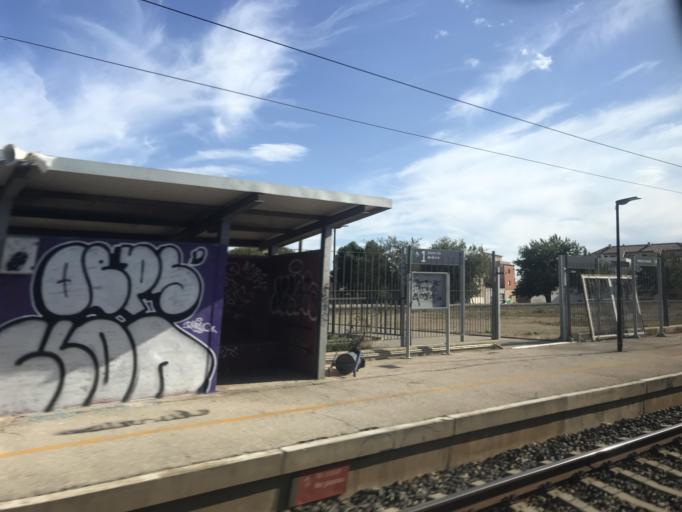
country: ES
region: Catalonia
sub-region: Provincia de Tarragona
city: Camarles
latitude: 40.7753
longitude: 0.6713
